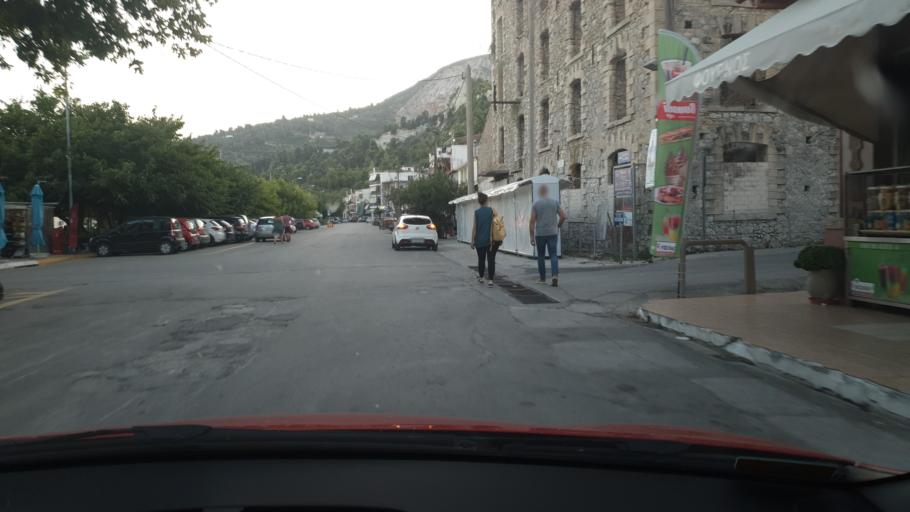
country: GR
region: Central Greece
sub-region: Nomos Evvoias
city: Kymi
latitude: 38.6313
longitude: 24.1243
